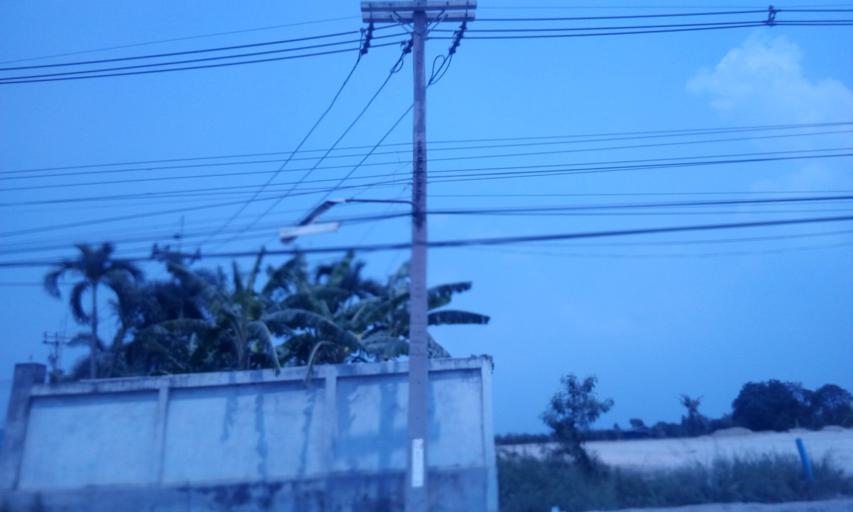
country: TH
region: Chon Buri
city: Phanat Nikhom
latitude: 13.4973
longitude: 101.1632
